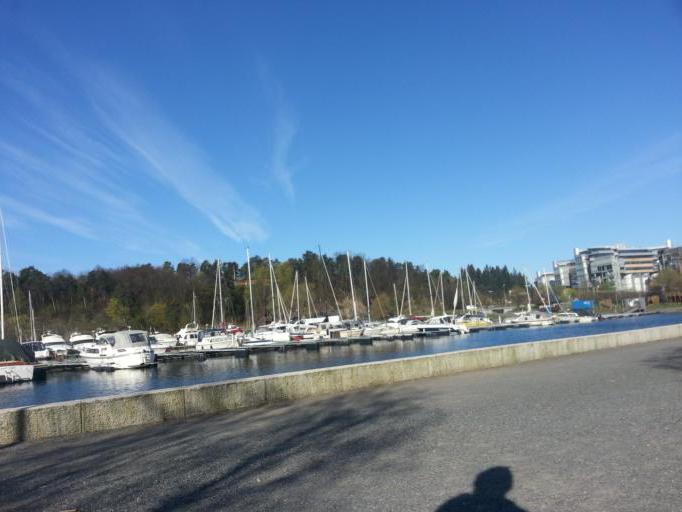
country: NO
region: Oslo
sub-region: Oslo
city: Sjolyststranda
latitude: 59.9168
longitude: 10.6911
